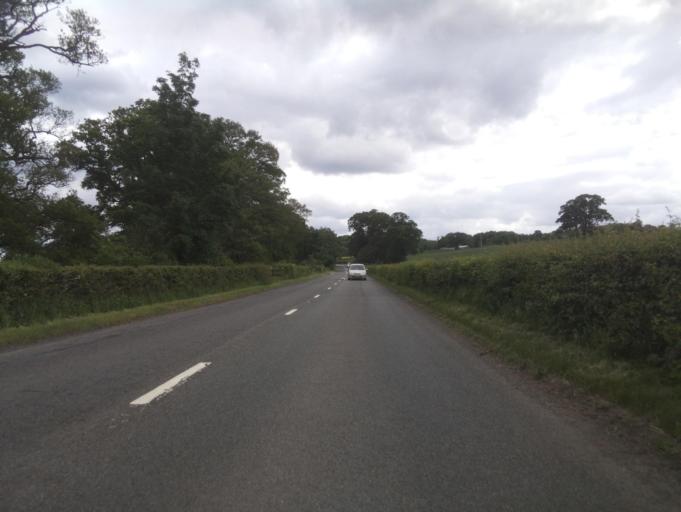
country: GB
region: England
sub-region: Herefordshire
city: Yatton
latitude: 51.9902
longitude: -2.5052
